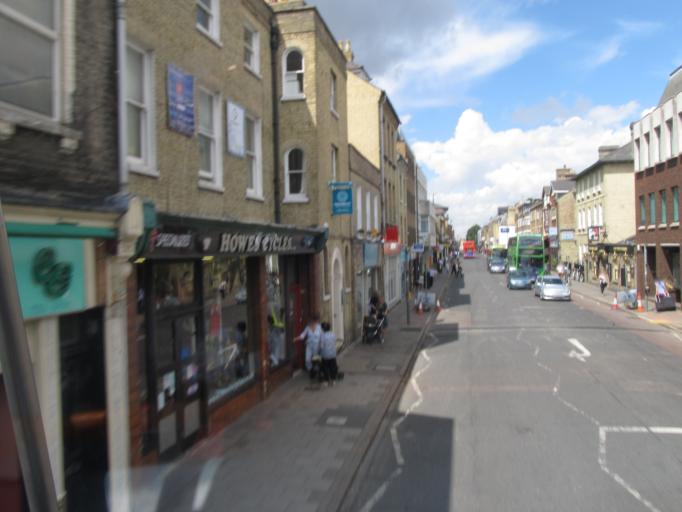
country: GB
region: England
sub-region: Cambridgeshire
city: Cambridge
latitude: 52.1993
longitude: 0.1273
